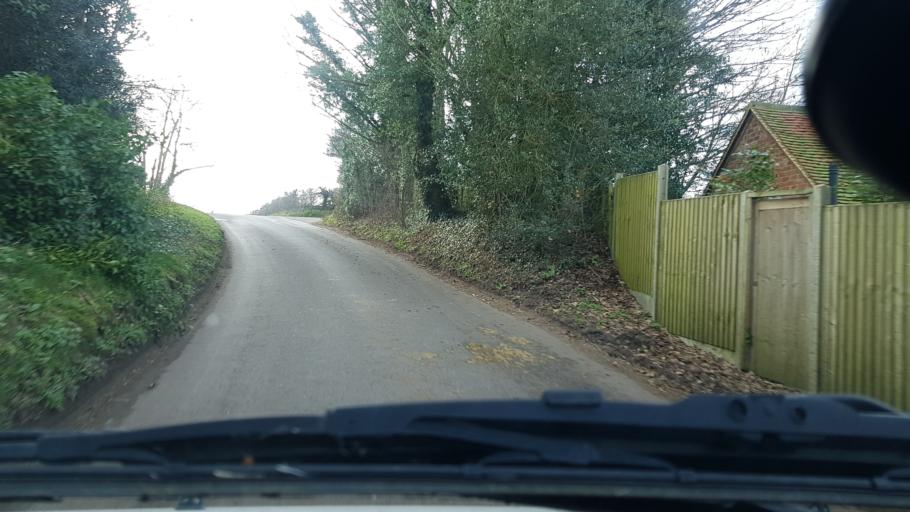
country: GB
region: England
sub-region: Surrey
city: Cobham
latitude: 51.3080
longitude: -0.4347
